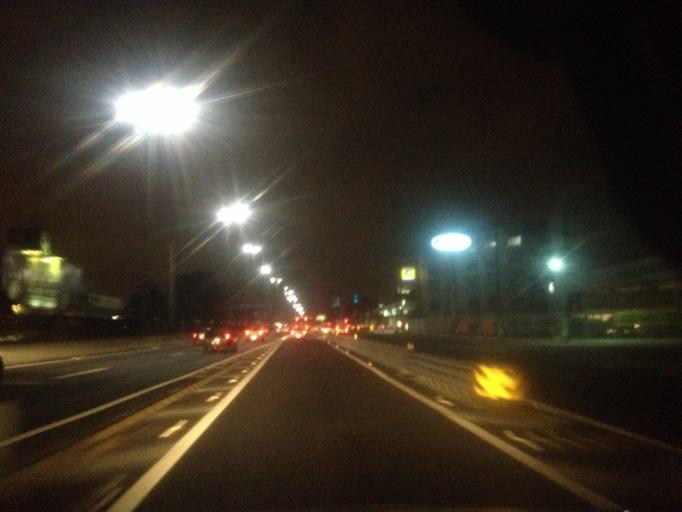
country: BR
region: Rio de Janeiro
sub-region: Sao Joao De Meriti
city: Sao Joao de Meriti
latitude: -22.7957
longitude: -43.3613
